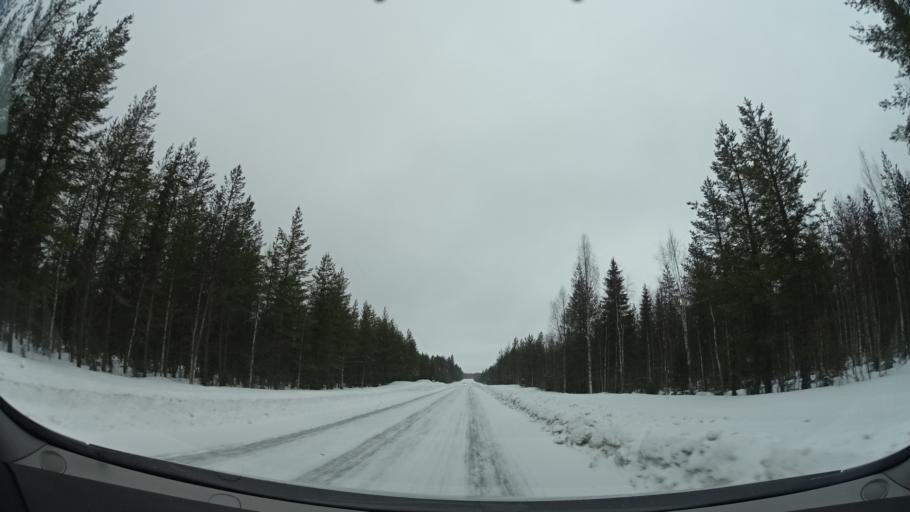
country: SE
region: Vaesterbotten
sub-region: Mala Kommun
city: Mala
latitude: 65.1149
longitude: 18.8858
